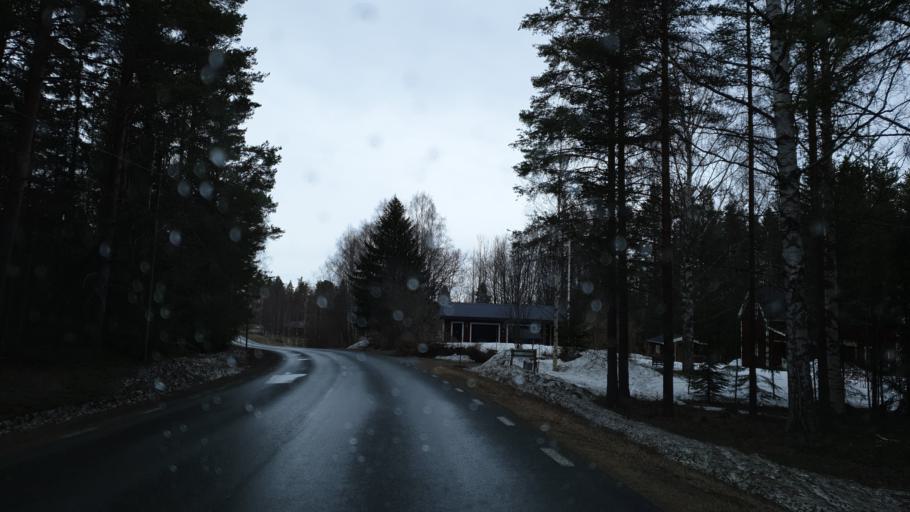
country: SE
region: Vaesterbotten
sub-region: Skelleftea Kommun
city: Kage
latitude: 64.8275
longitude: 20.9878
